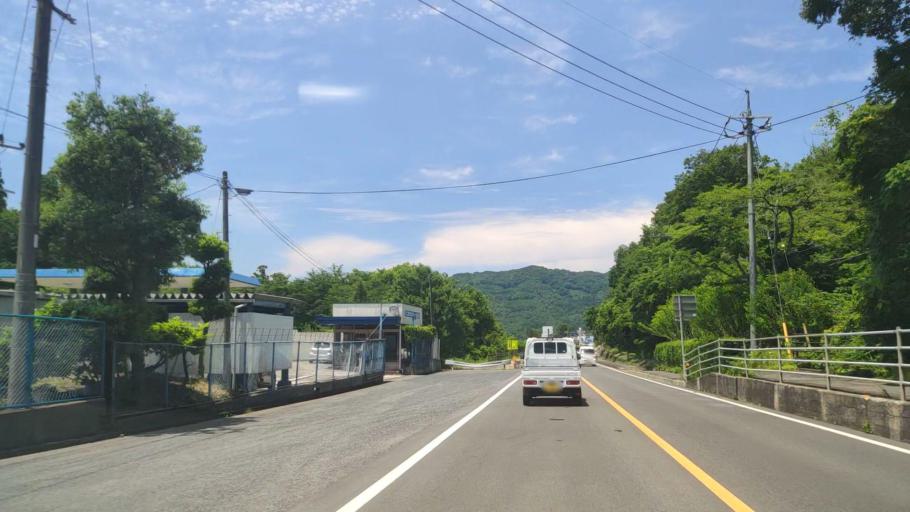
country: JP
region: Tottori
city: Tottori
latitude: 35.4044
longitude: 134.2578
